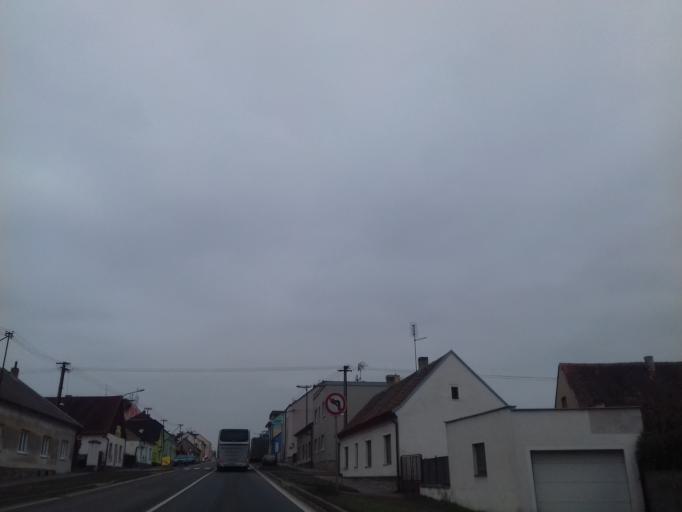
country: CZ
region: Plzensky
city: Line
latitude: 49.6966
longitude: 13.2604
